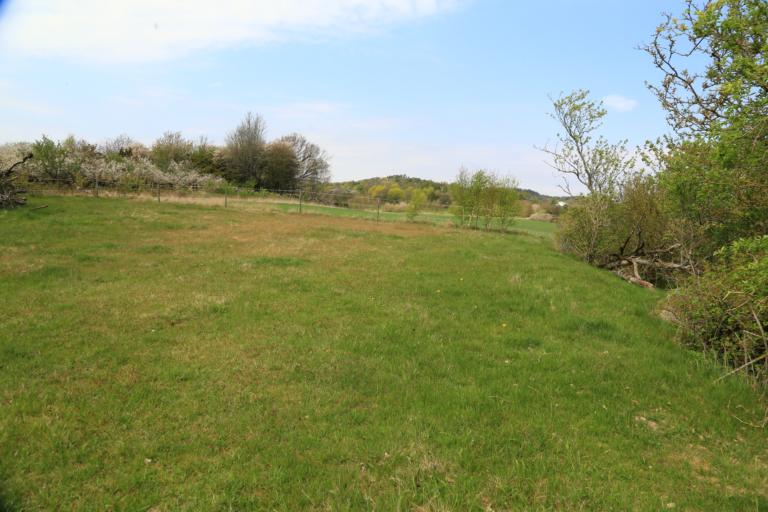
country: SE
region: Halland
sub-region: Varbergs Kommun
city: Varberg
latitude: 57.1305
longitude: 12.3010
